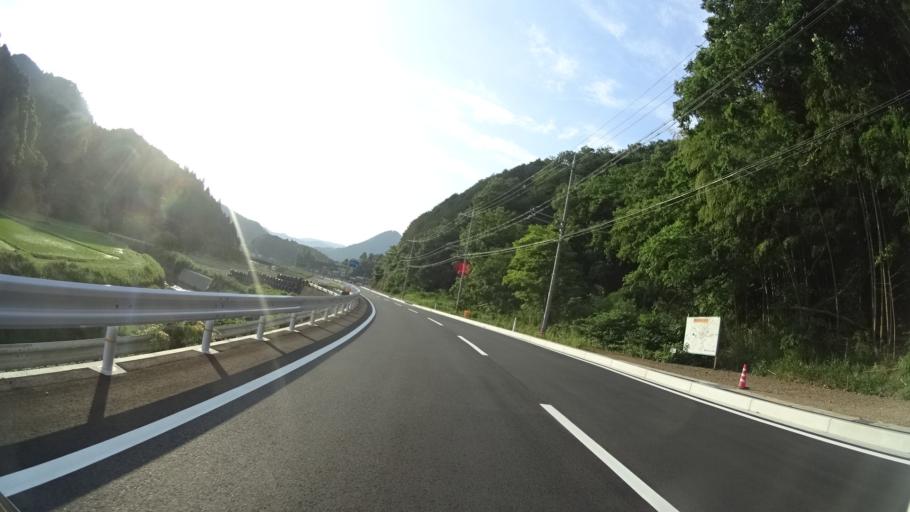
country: JP
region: Kyoto
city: Miyazu
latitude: 35.4281
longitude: 135.2154
